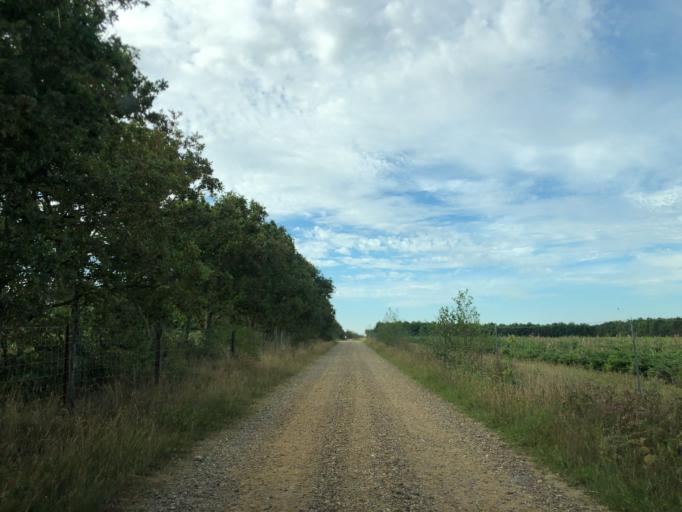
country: DK
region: Central Jutland
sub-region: Ringkobing-Skjern Kommune
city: Skjern
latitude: 56.0815
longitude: 8.4235
